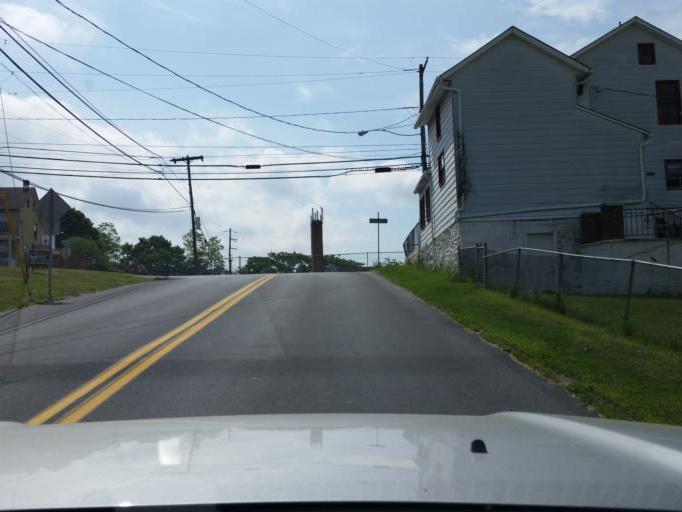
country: US
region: Pennsylvania
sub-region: Dauphin County
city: Enhaut
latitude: 40.2358
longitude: -76.8237
